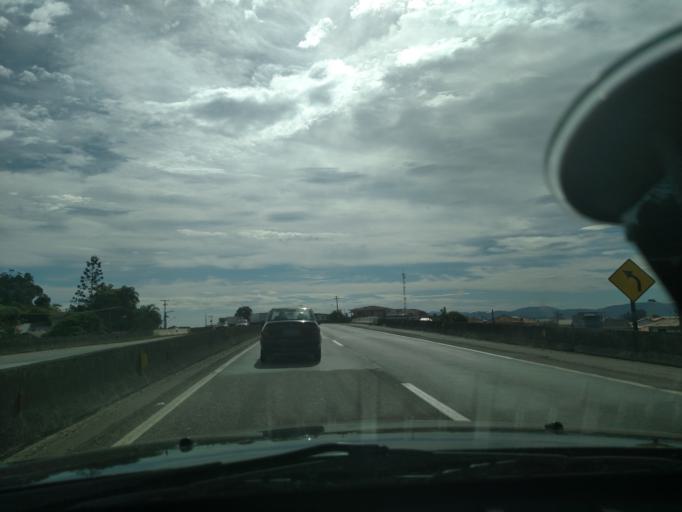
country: BR
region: Santa Catarina
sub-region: Biguacu
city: Biguacu
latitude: -27.4873
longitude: -48.6505
